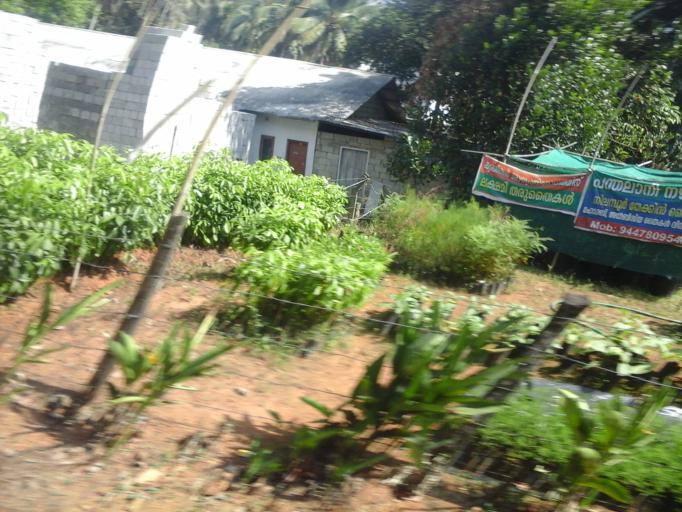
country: IN
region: Kerala
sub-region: Kottayam
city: Erattupetta
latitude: 9.7018
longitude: 76.7574
